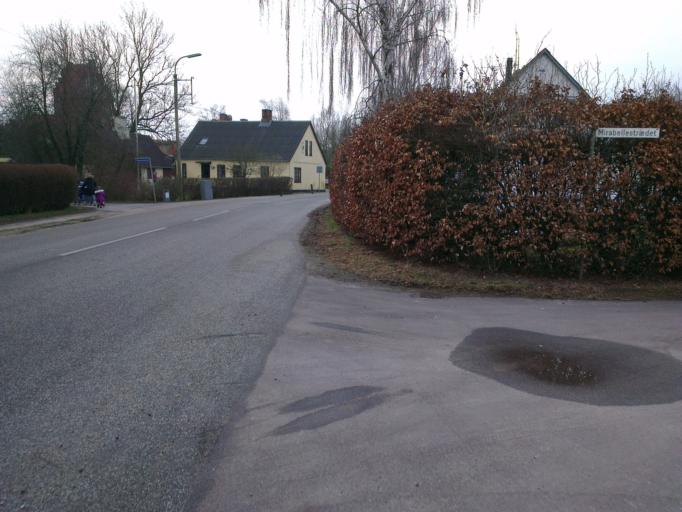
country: DK
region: Capital Region
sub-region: Frederikssund Kommune
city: Skibby
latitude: 55.7619
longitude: 11.9117
